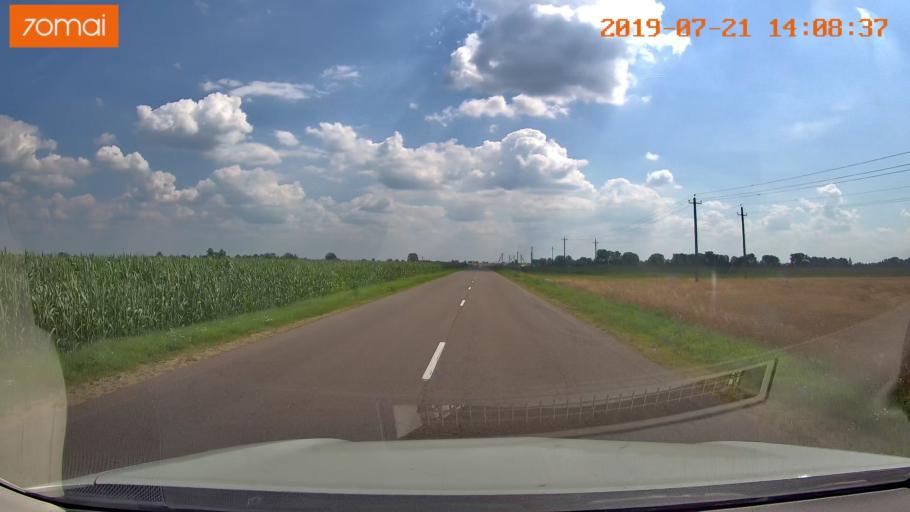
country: BY
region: Grodnenskaya
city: Lyubcha
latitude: 53.6719
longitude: 26.1273
